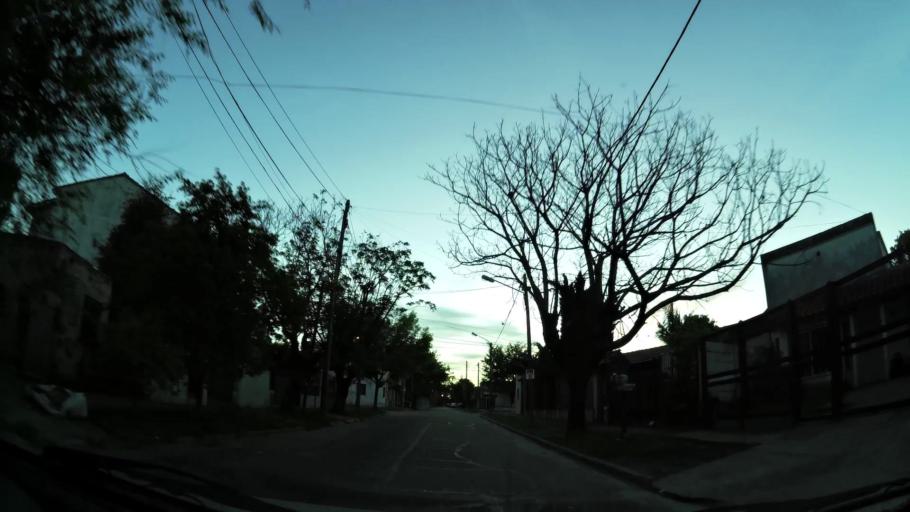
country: AR
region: Buenos Aires
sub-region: Partido de Quilmes
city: Quilmes
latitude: -34.7692
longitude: -58.1995
